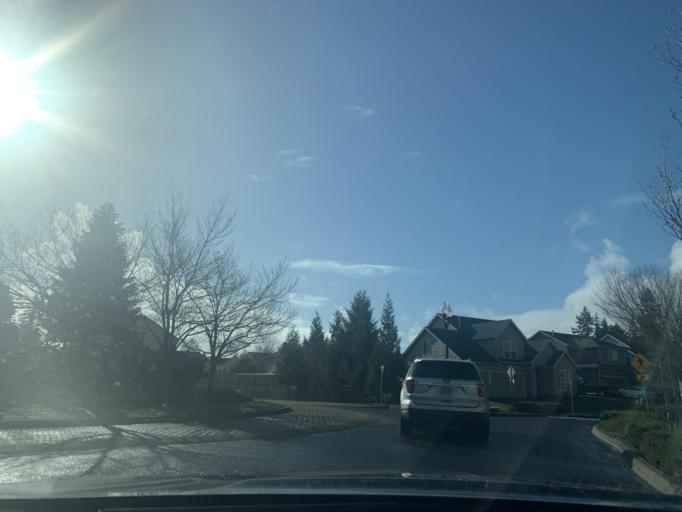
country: US
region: Oregon
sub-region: Washington County
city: Sherwood
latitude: 45.3592
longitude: -122.8565
